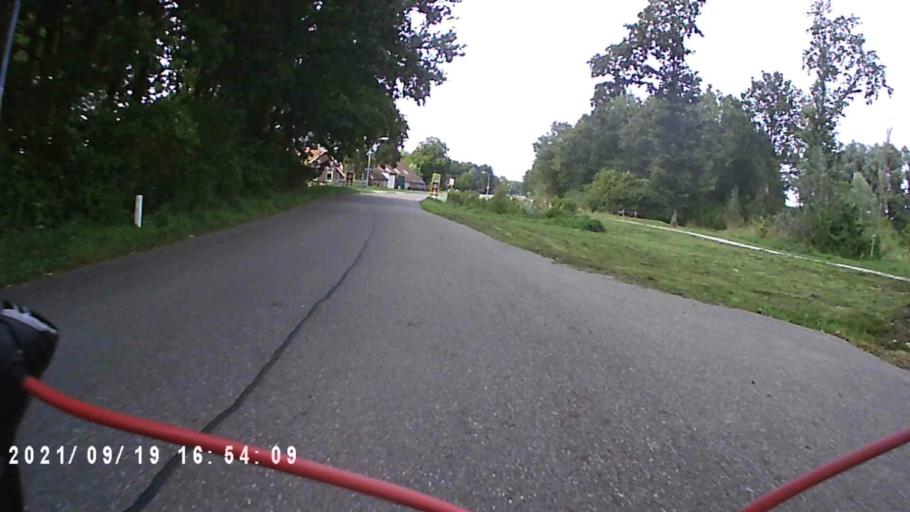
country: NL
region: Groningen
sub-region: Gemeente  Oldambt
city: Winschoten
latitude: 53.1860
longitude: 7.0782
